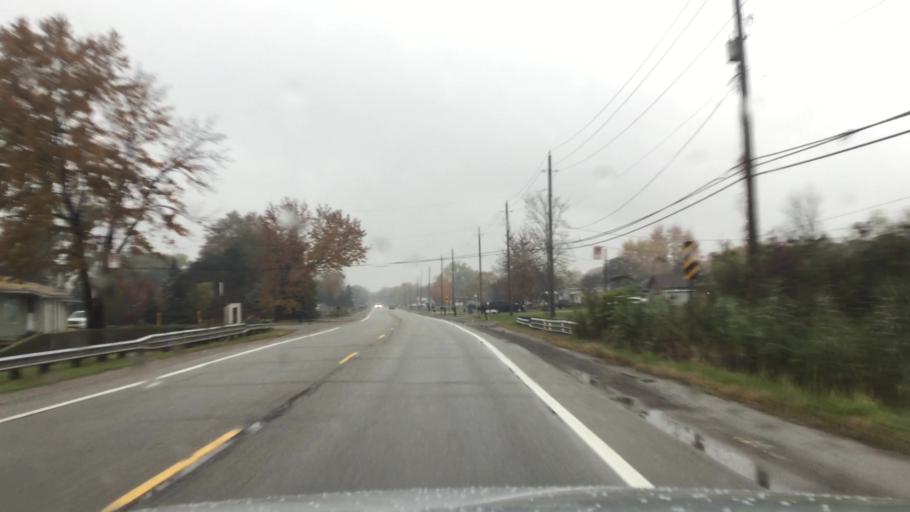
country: US
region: Michigan
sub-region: Macomb County
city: New Baltimore
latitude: 42.6573
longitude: -82.7878
